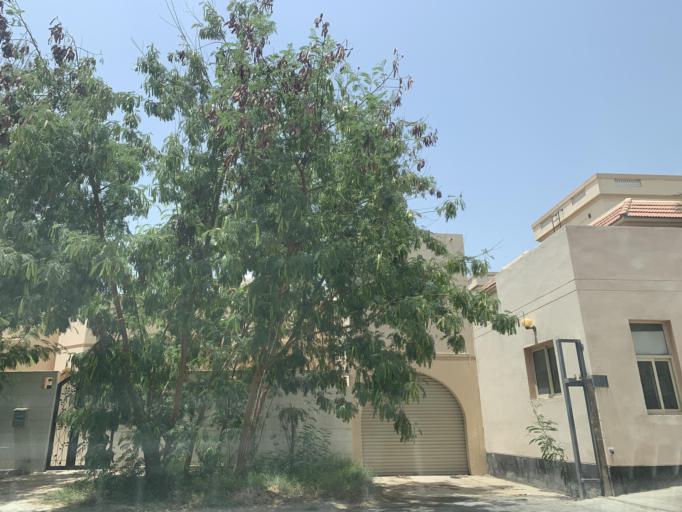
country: BH
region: Northern
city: Madinat `Isa
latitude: 26.1706
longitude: 50.5698
